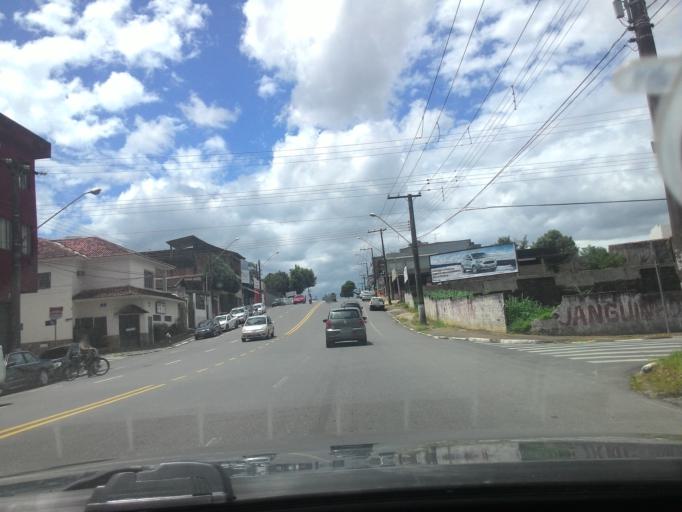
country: BR
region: Sao Paulo
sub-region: Registro
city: Registro
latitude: -24.5021
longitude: -47.8410
